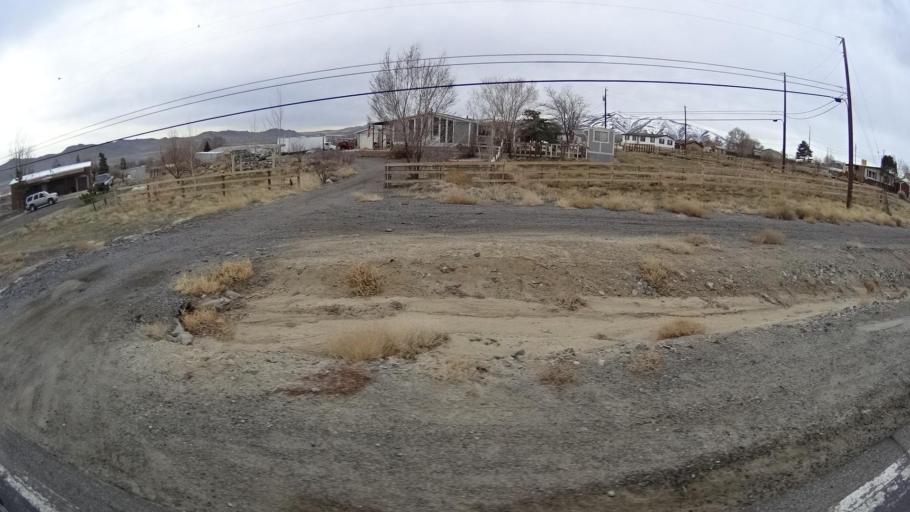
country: US
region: Nevada
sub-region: Washoe County
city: Lemmon Valley
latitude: 39.6763
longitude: -119.8537
